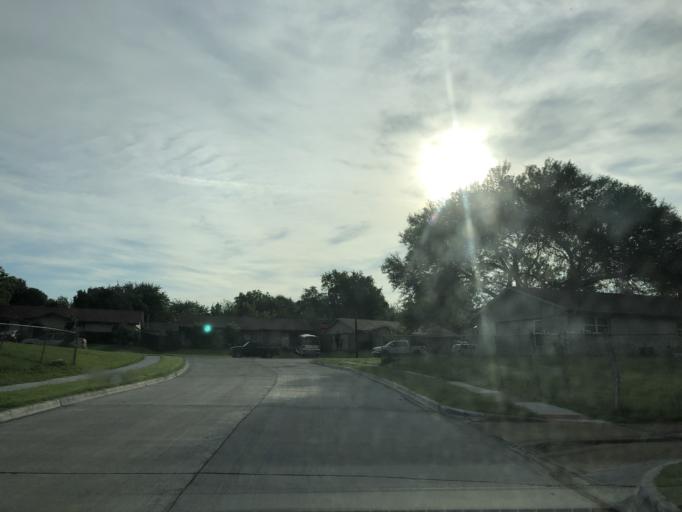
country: US
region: Texas
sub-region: Dallas County
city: Sunnyvale
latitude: 32.8478
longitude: -96.6011
